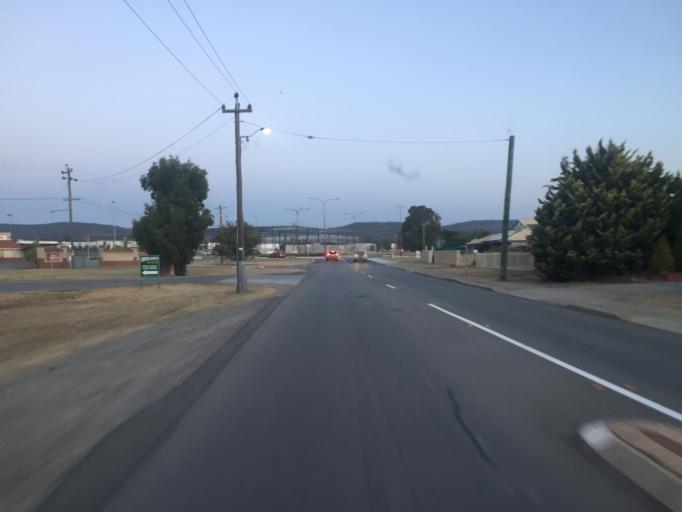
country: AU
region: Western Australia
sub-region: Gosnells
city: Maddington
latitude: -32.0322
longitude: 115.9945
